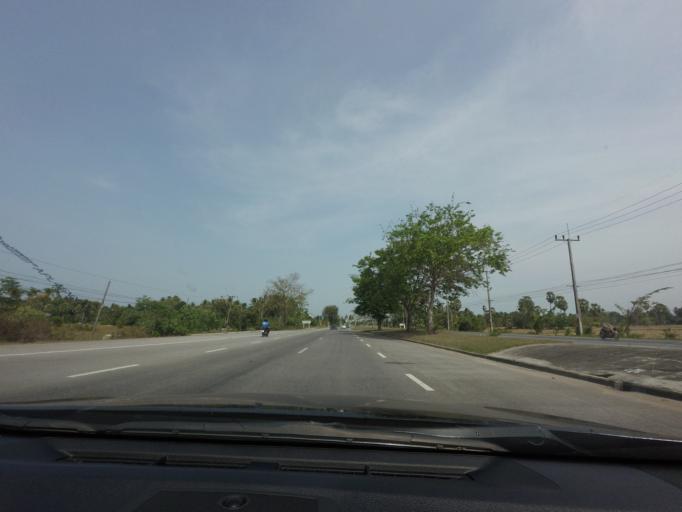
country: TH
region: Pattani
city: Yaring
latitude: 6.8218
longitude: 101.4040
